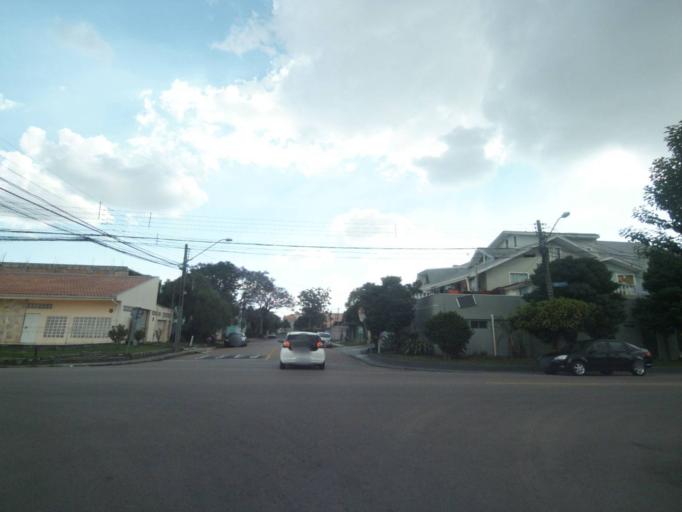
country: BR
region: Parana
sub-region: Sao Jose Dos Pinhais
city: Sao Jose dos Pinhais
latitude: -25.5314
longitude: -49.2651
